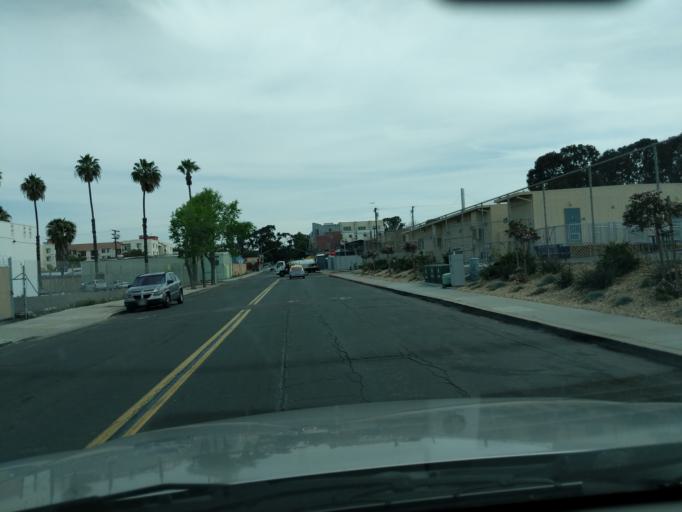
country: US
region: California
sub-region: San Diego County
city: San Diego
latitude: 32.7016
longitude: -117.1497
